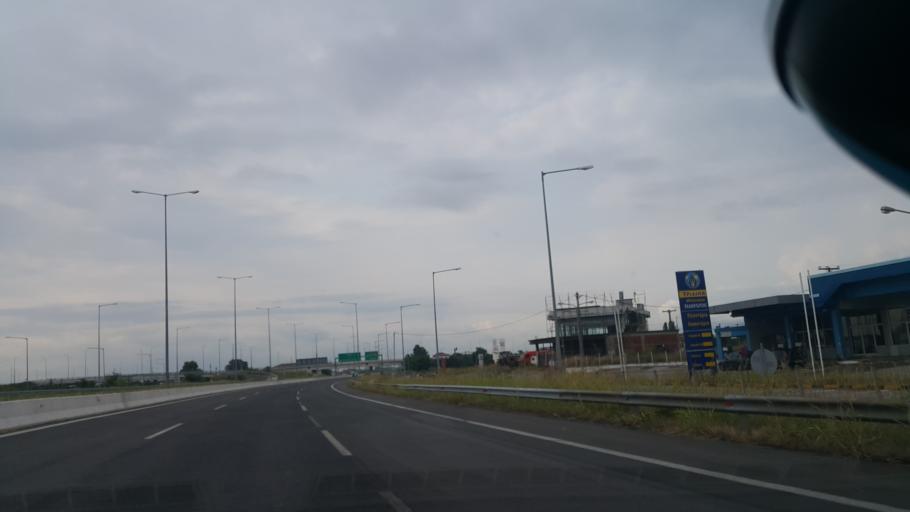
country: GR
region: Central Macedonia
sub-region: Nomos Pierias
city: Peristasi
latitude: 40.2596
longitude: 22.5301
